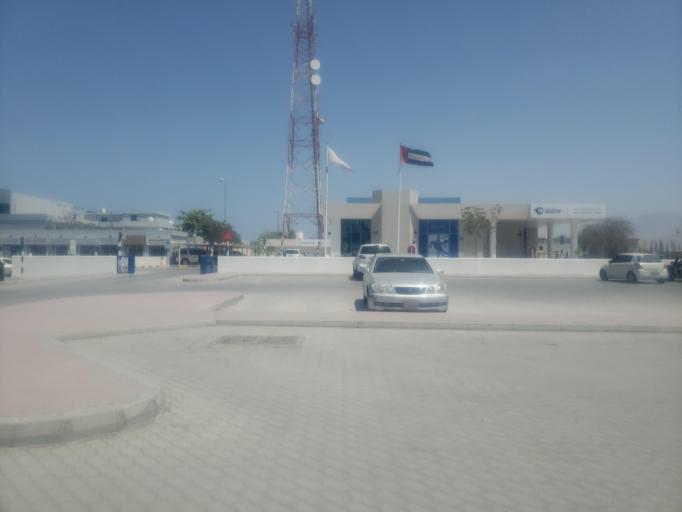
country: AE
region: Ra's al Khaymah
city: Ras al-Khaimah
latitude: 25.8022
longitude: 55.9730
